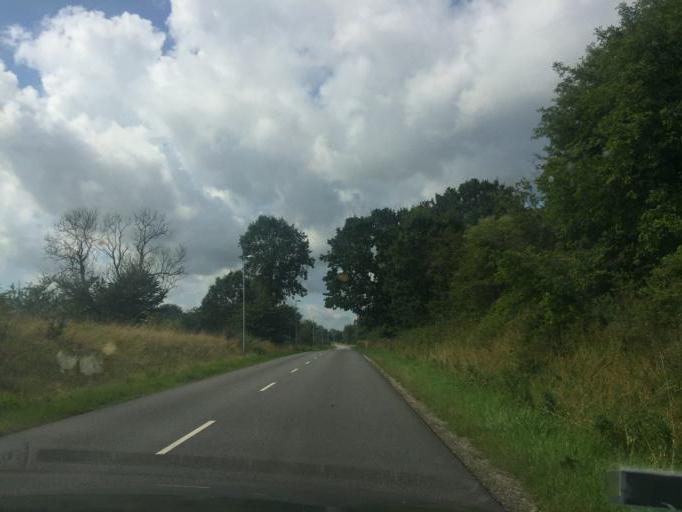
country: DK
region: Capital Region
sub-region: Allerod Kommune
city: Blovstrod
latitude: 55.8529
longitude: 12.3951
